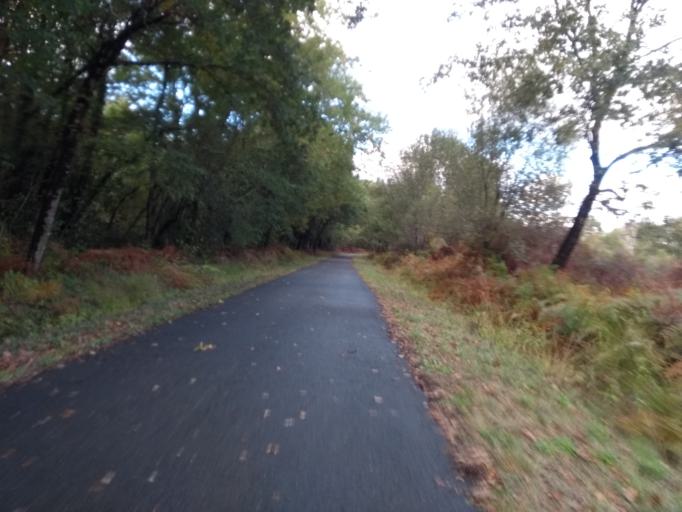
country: FR
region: Aquitaine
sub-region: Departement de la Gironde
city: Saint-Aubin-de-Medoc
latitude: 44.7988
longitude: -0.7073
